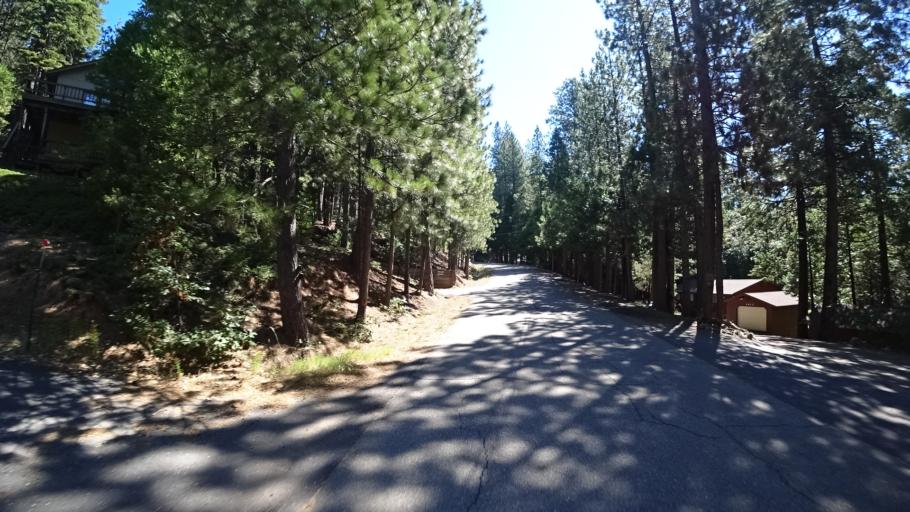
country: US
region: California
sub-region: Calaveras County
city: Arnold
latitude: 38.2828
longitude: -120.2818
